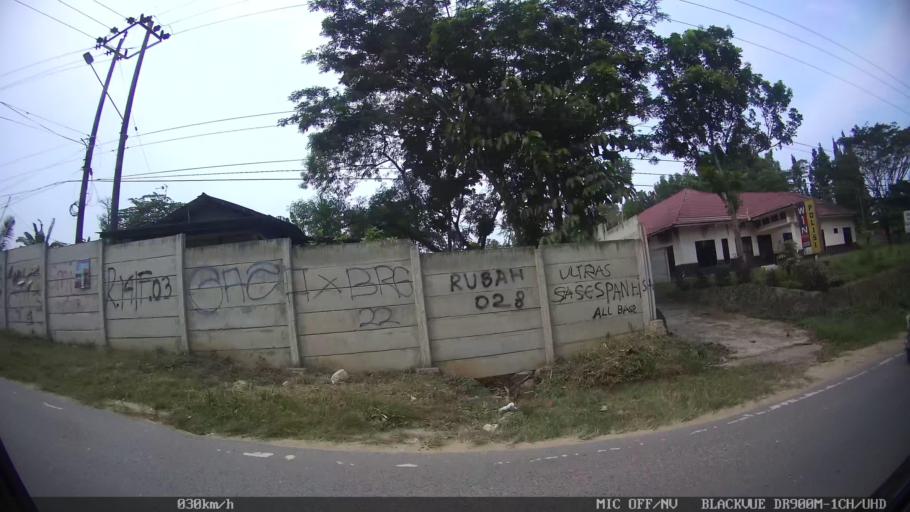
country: ID
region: Lampung
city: Kedaton
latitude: -5.4027
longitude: 105.3155
